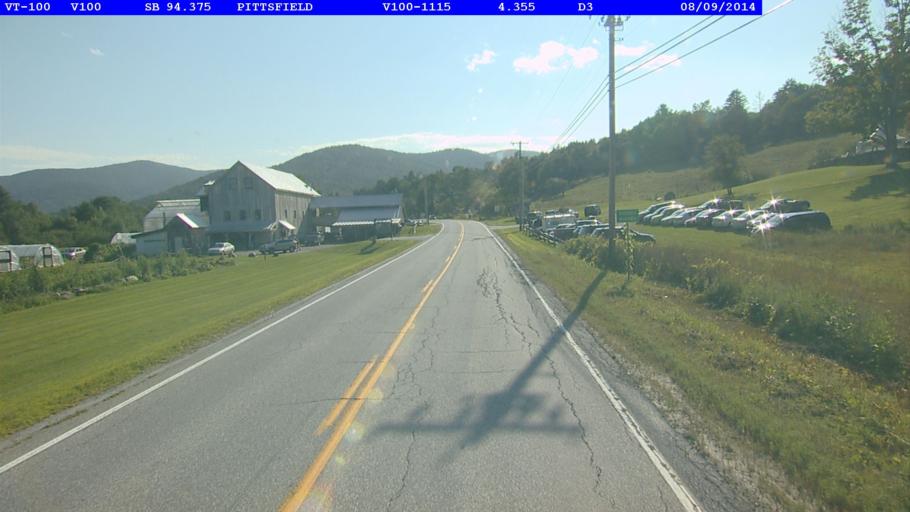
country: US
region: Vermont
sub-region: Orange County
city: Randolph
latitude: 43.7768
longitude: -72.8081
